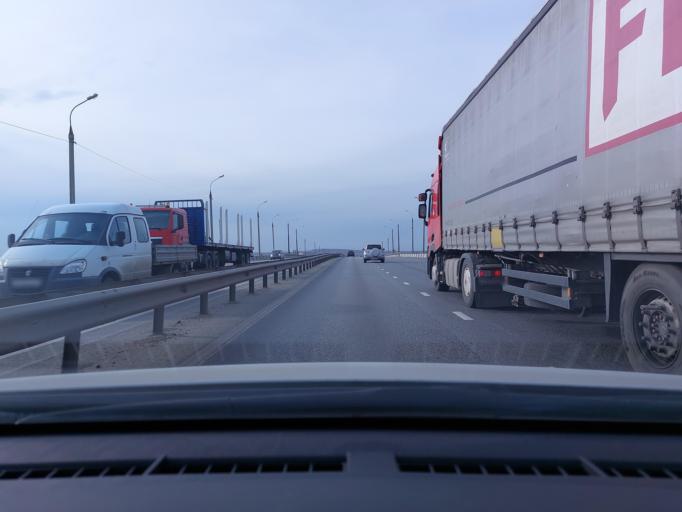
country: RU
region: Irkutsk
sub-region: Irkutskiy Rayon
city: Irkutsk
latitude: 52.3253
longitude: 104.2279
